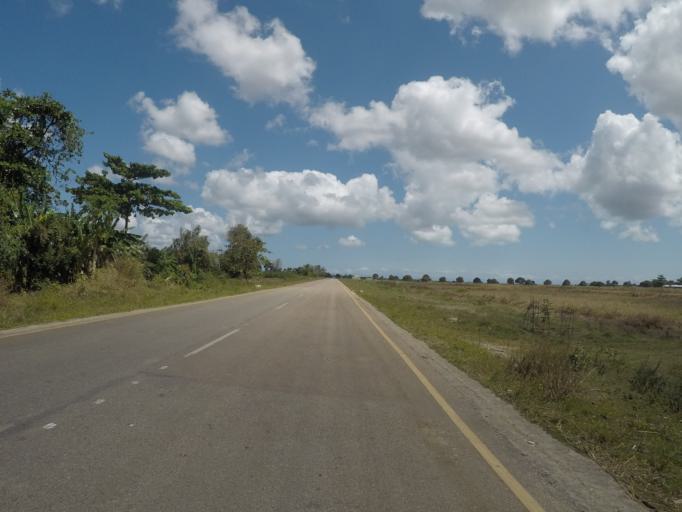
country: TZ
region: Zanzibar Central/South
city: Koani
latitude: -6.1847
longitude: 39.3717
